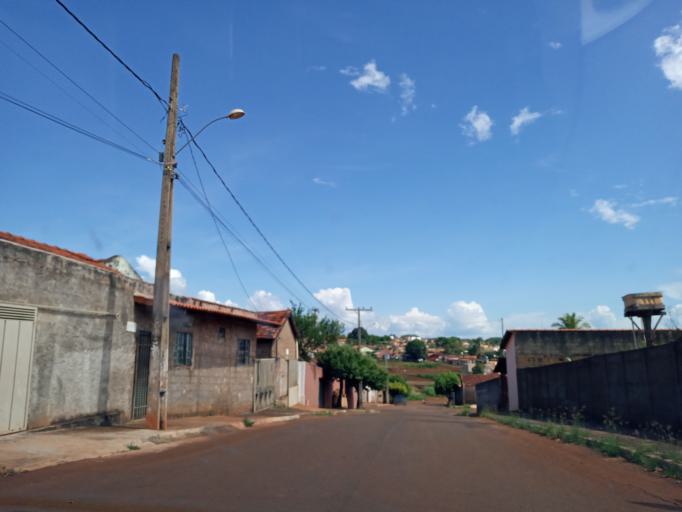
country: BR
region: Goias
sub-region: Itumbiara
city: Itumbiara
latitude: -18.4326
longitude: -49.1846
